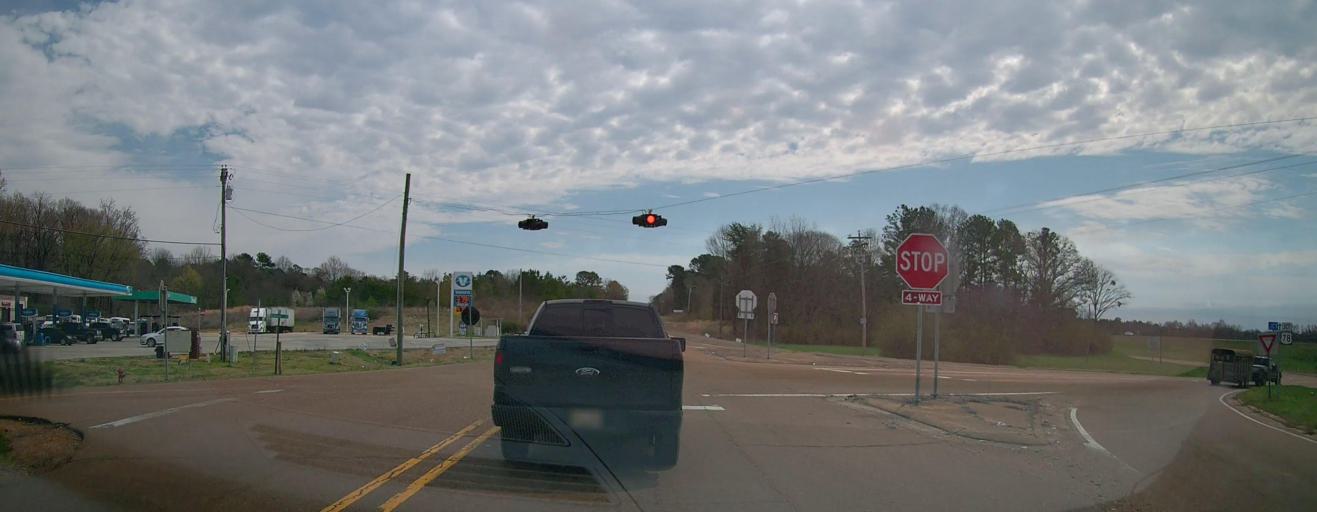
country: US
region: Mississippi
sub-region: Marshall County
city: Holly Springs
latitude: 34.8281
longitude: -89.5649
